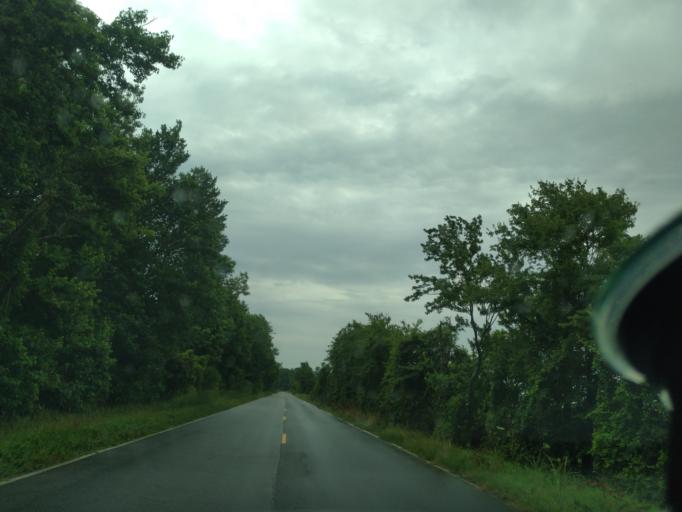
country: US
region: North Carolina
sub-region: Washington County
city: Plymouth
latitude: 35.8302
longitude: -76.5202
